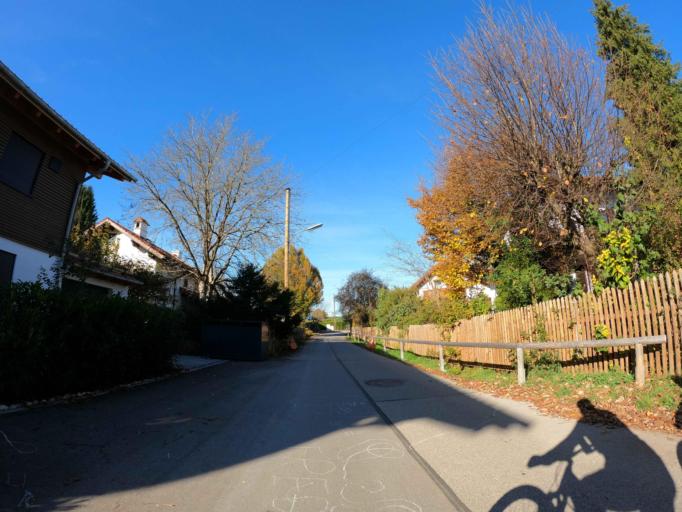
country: DE
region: Bavaria
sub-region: Upper Bavaria
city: Oberhaching
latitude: 48.0288
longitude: 11.5961
